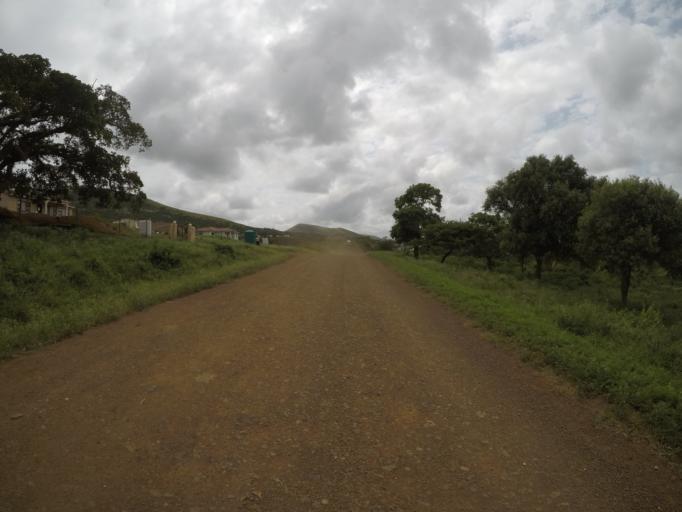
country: ZA
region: KwaZulu-Natal
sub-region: uThungulu District Municipality
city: Empangeni
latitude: -28.5930
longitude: 31.8820
